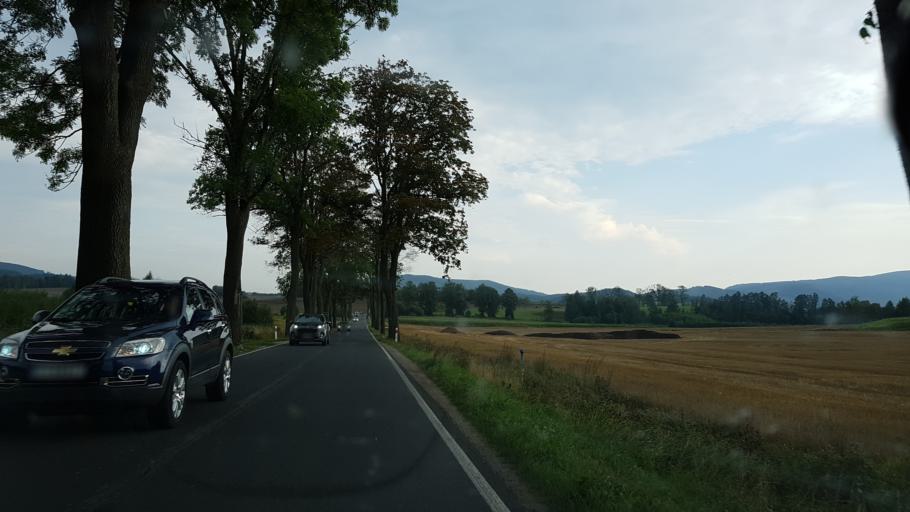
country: PL
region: Lower Silesian Voivodeship
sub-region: Powiat kamiennogorski
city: Marciszow
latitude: 50.8764
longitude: 15.9997
